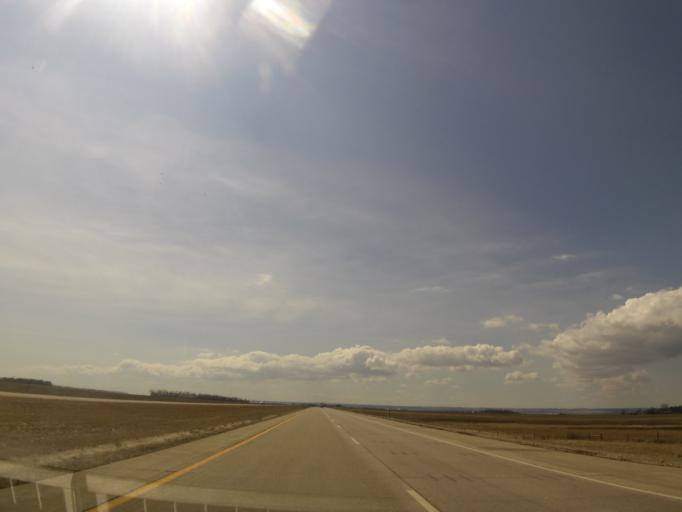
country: US
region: South Dakota
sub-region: Roberts County
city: Sisseton
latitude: 45.7155
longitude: -96.9539
